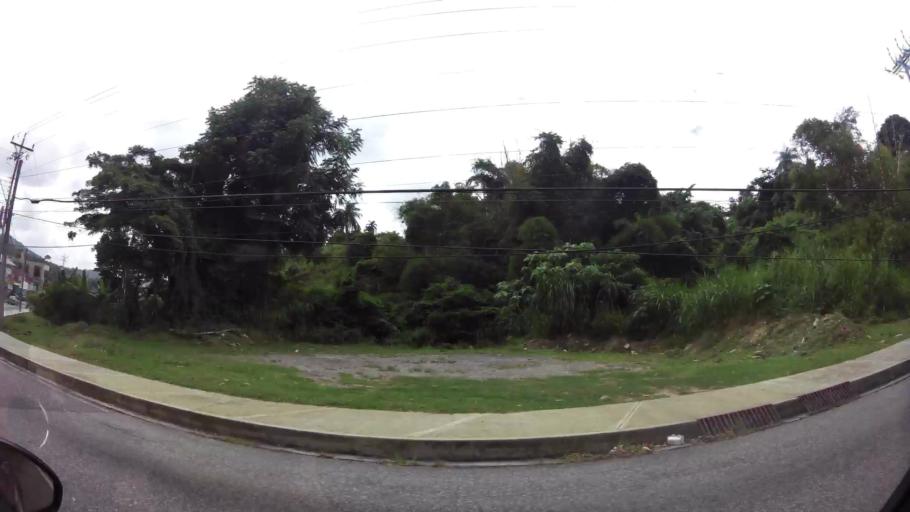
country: TT
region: Diego Martin
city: Petit Valley
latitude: 10.6819
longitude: -61.5298
